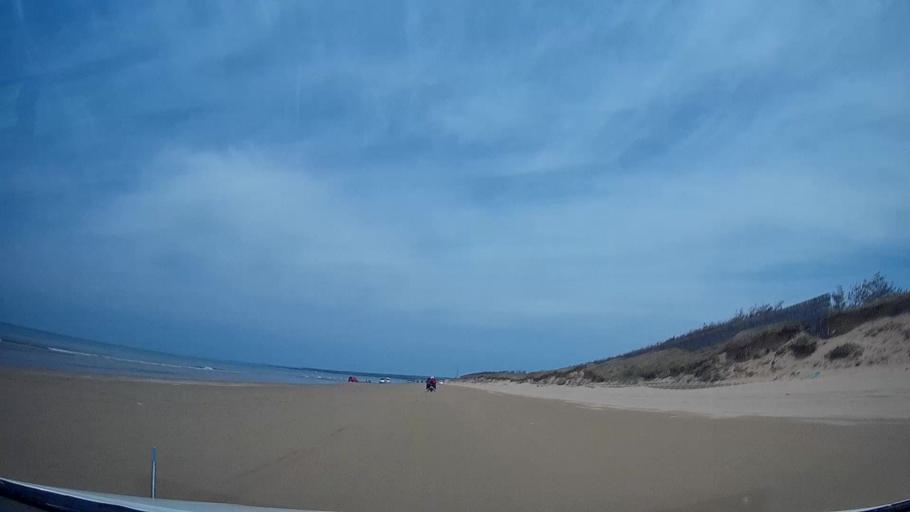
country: JP
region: Ishikawa
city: Hakui
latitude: 36.8572
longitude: 136.7555
